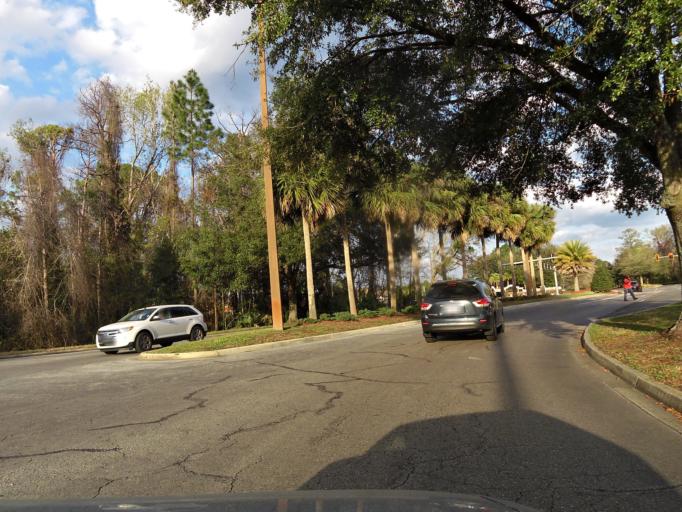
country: US
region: Florida
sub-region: Saint Johns County
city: Fruit Cove
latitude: 30.1904
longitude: -81.5528
